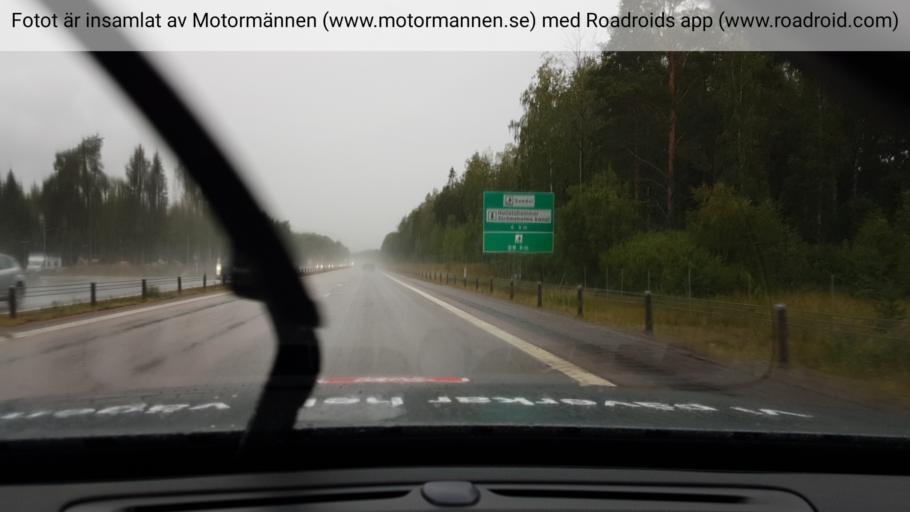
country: SE
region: Vaestmanland
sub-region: Vasteras
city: Skultuna
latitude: 59.5904
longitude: 16.4046
